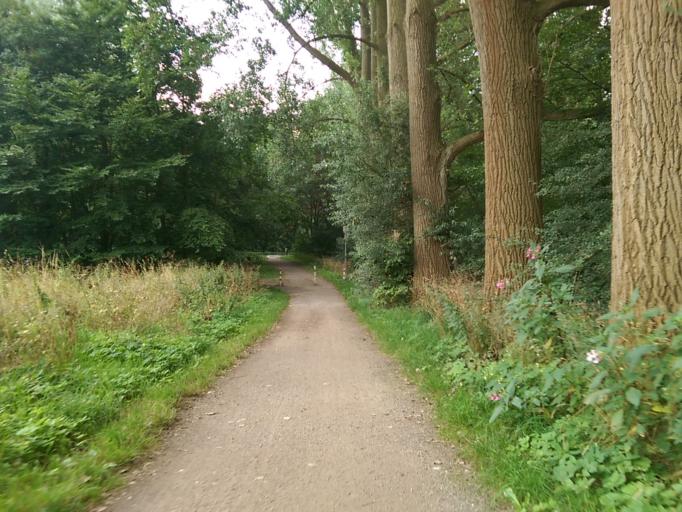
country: DE
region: North Rhine-Westphalia
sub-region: Regierungsbezirk Detmold
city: Guetersloh
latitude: 51.9364
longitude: 8.3533
